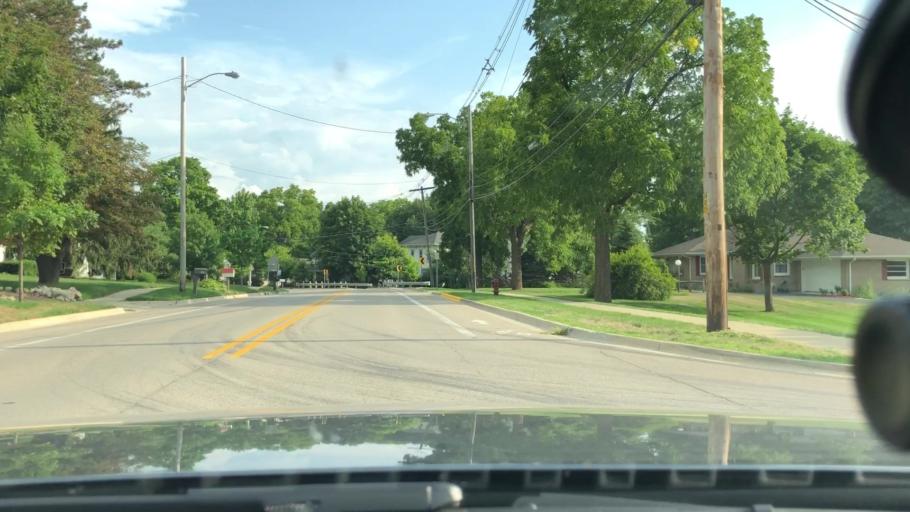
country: US
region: Michigan
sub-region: Washtenaw County
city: Manchester
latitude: 42.1542
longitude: -84.0410
